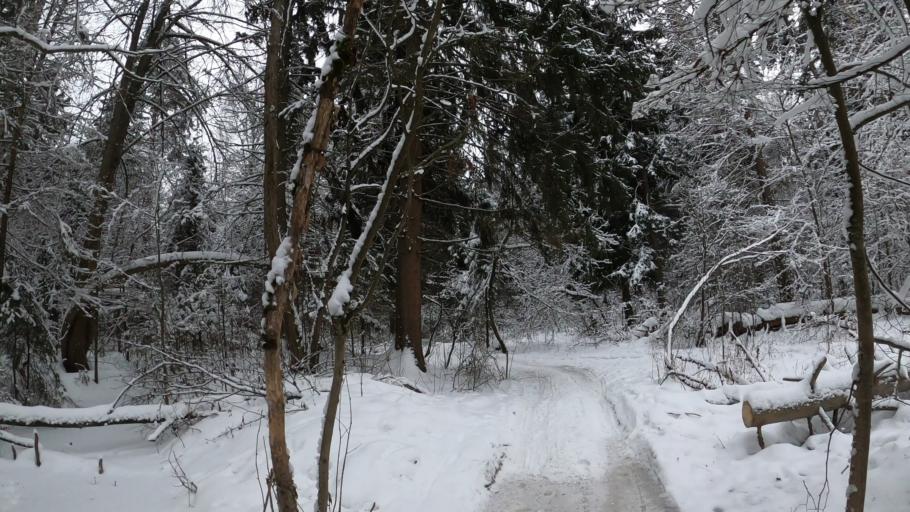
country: RU
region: Moskovskaya
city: Firsanovka
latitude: 55.9336
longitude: 37.2214
